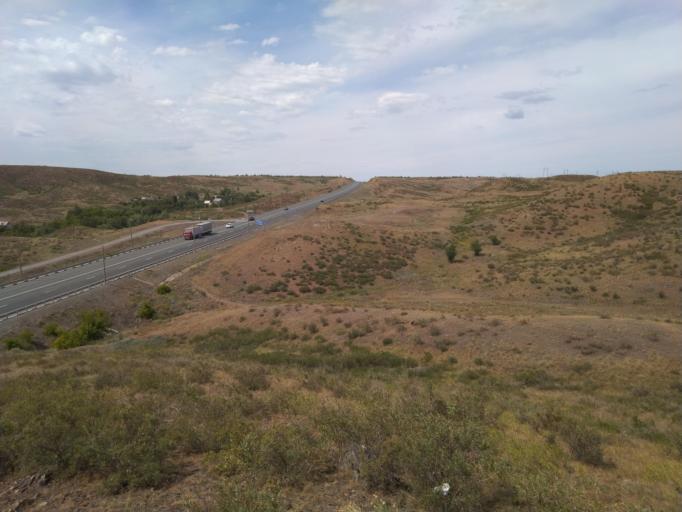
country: RU
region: Orenburg
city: Novotroitsk
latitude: 51.2038
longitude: 58.4366
